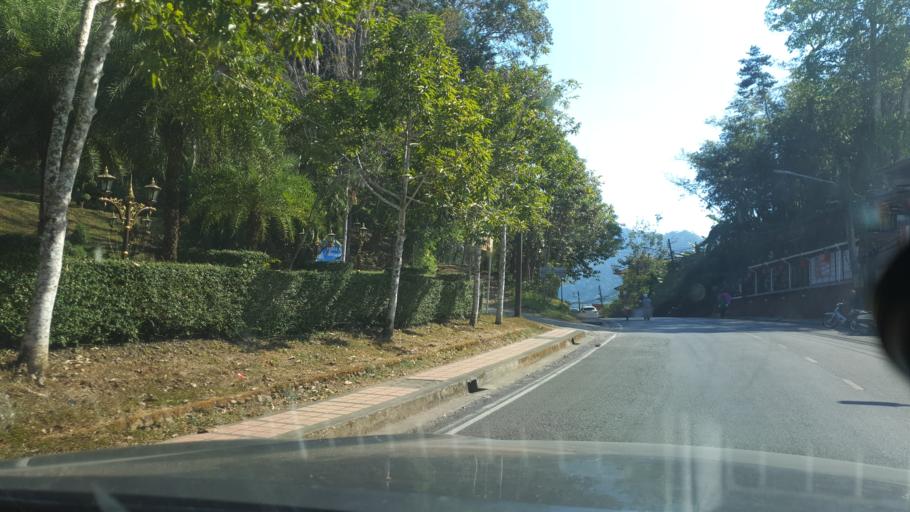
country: TH
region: Ranong
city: Ranong
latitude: 9.9647
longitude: 98.6366
